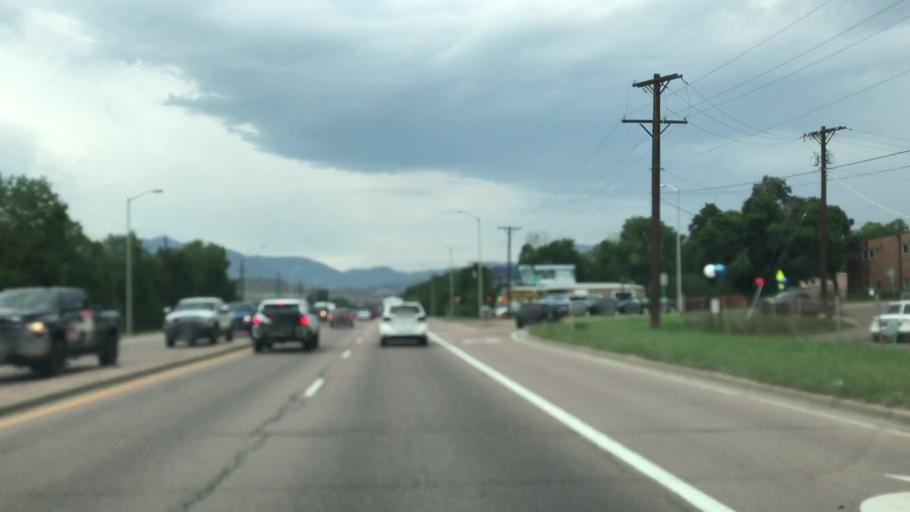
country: US
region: Colorado
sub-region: El Paso County
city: Colorado Springs
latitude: 38.8353
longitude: -104.8487
